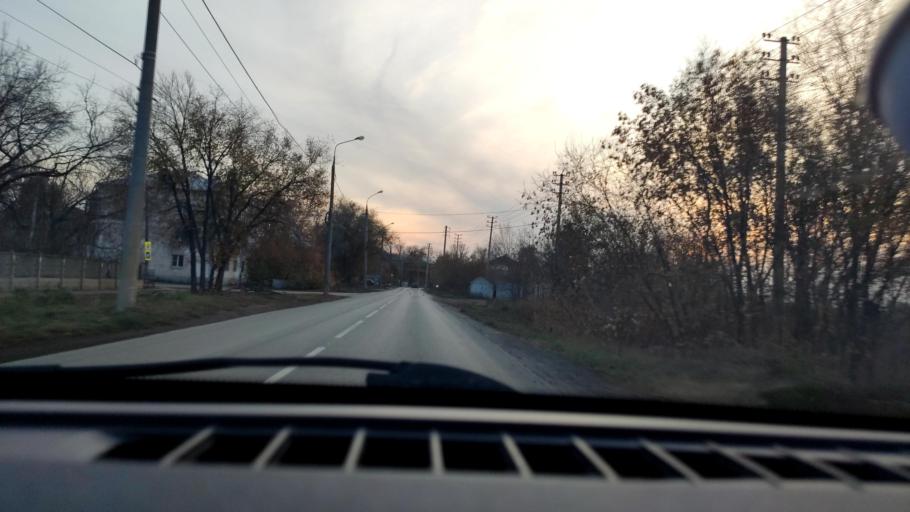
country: RU
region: Samara
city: Samara
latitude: 53.1389
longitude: 50.1278
